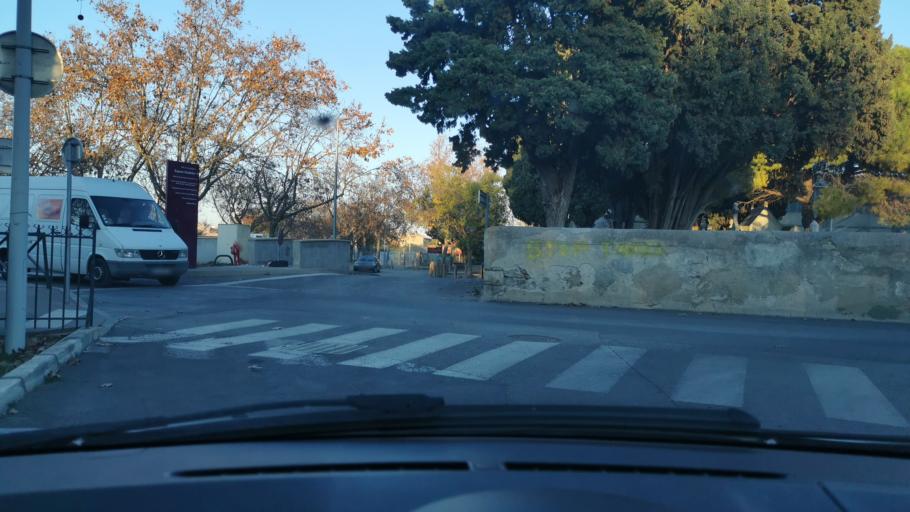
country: FR
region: Languedoc-Roussillon
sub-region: Departement de l'Herault
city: Frontignan
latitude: 43.4491
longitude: 3.7545
